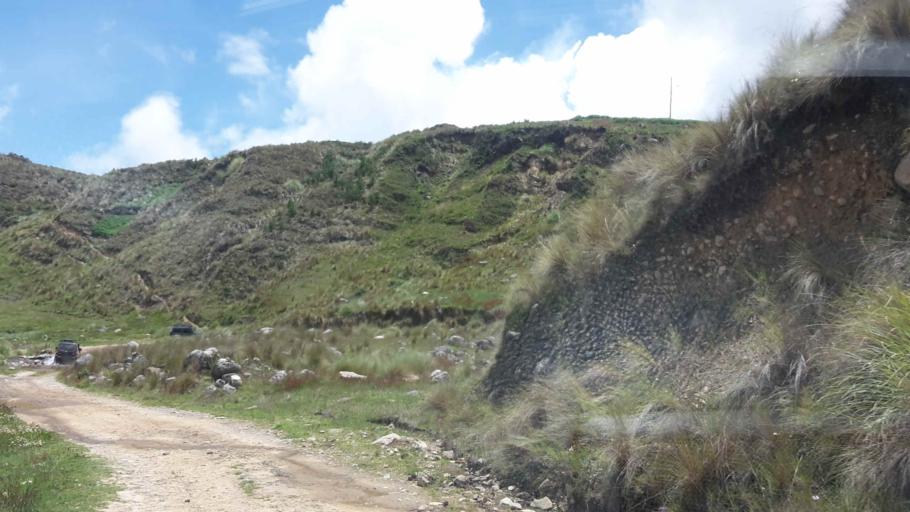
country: BO
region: Cochabamba
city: Cochabamba
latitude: -17.1830
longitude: -66.0617
